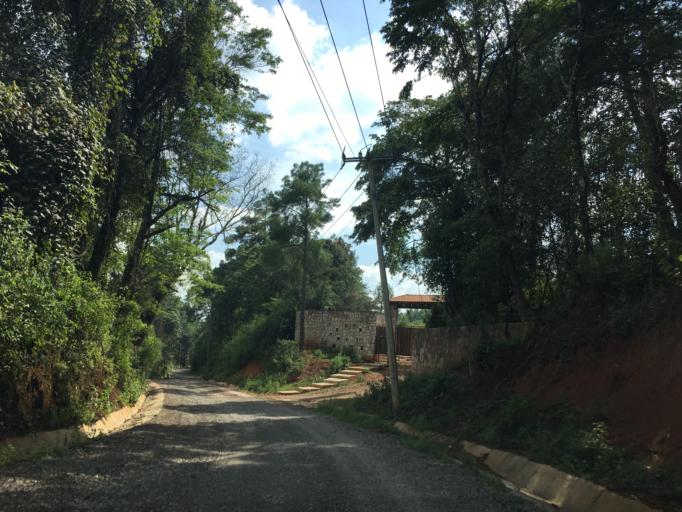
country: MX
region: Michoacan
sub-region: Morelia
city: Morelos
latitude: 19.5606
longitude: -101.1958
